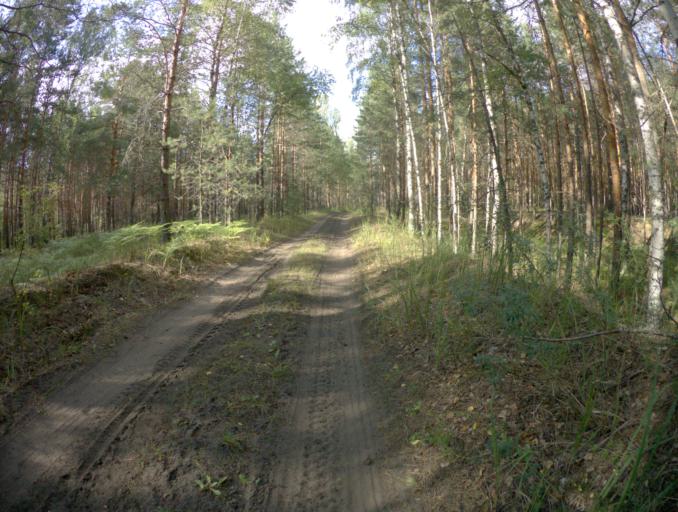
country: RU
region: Vladimir
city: Sobinka
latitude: 55.9508
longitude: 40.0589
